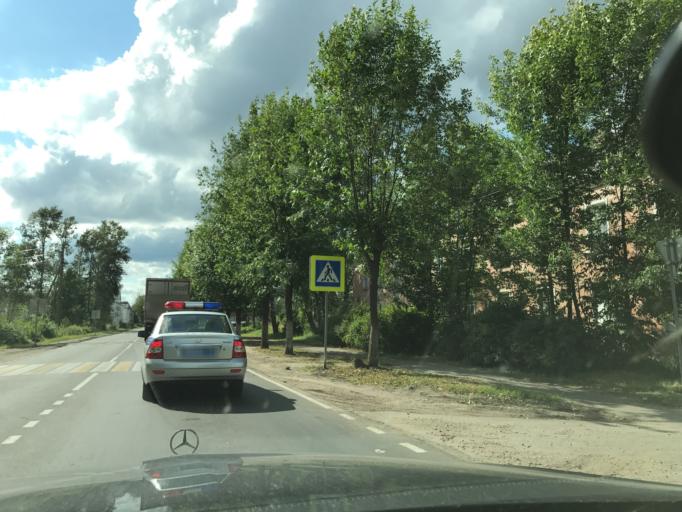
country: RU
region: Vladimir
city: Sobinka
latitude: 55.9972
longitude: 40.0323
